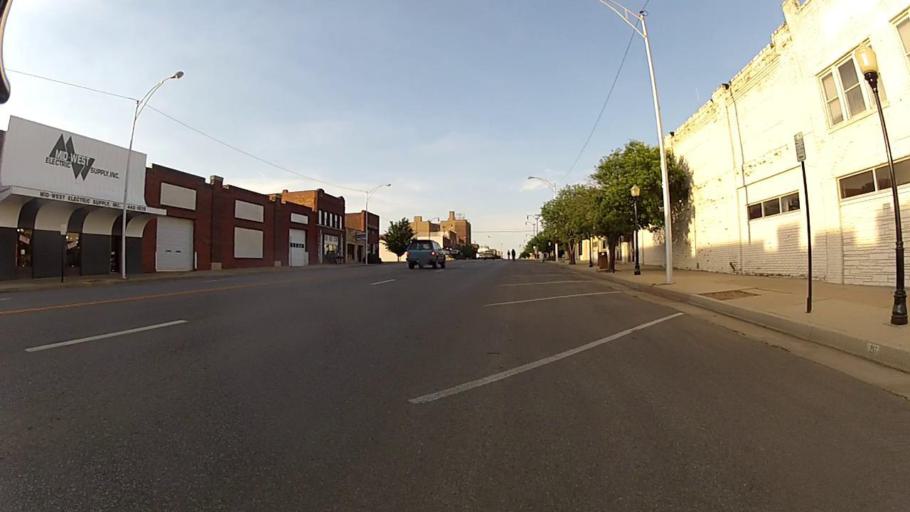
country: US
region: Kansas
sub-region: Cowley County
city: Arkansas City
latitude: 37.0642
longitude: -97.0392
